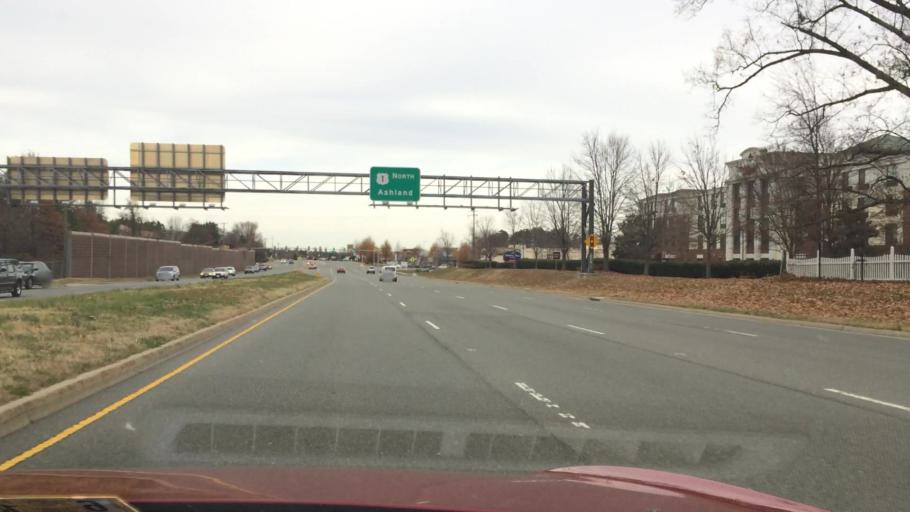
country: US
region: Virginia
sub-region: Henrico County
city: Glen Allen
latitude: 37.6634
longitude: -77.4603
